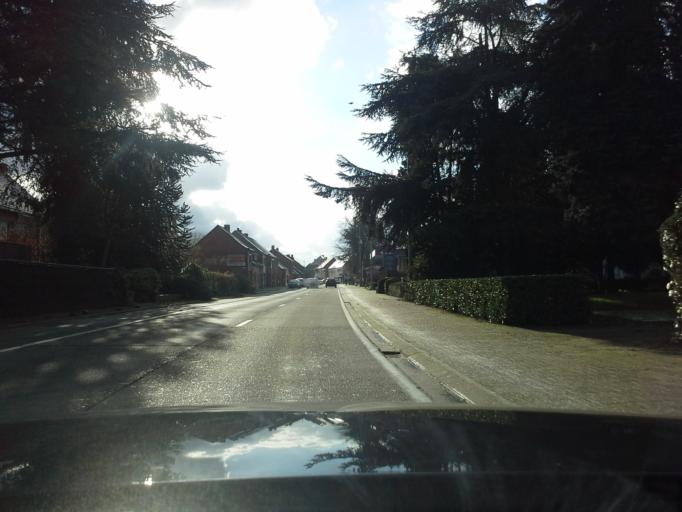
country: BE
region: Flanders
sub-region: Provincie Antwerpen
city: Meerhout
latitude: 51.1356
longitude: 5.0816
